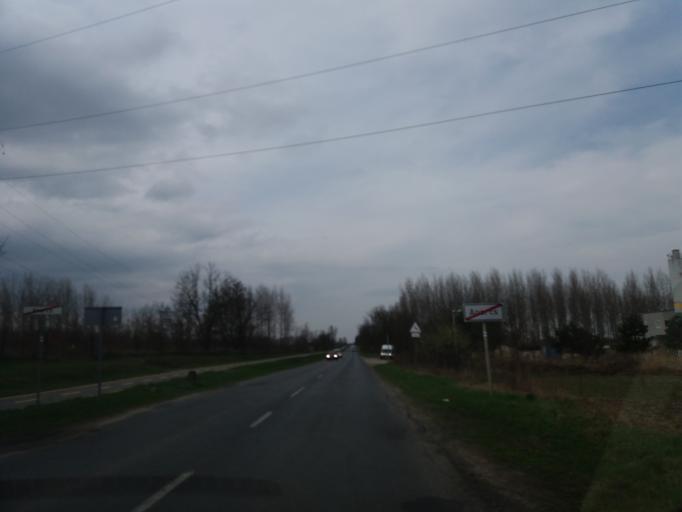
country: HU
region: Szabolcs-Szatmar-Bereg
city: Anarcs
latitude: 48.1874
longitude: 22.1017
